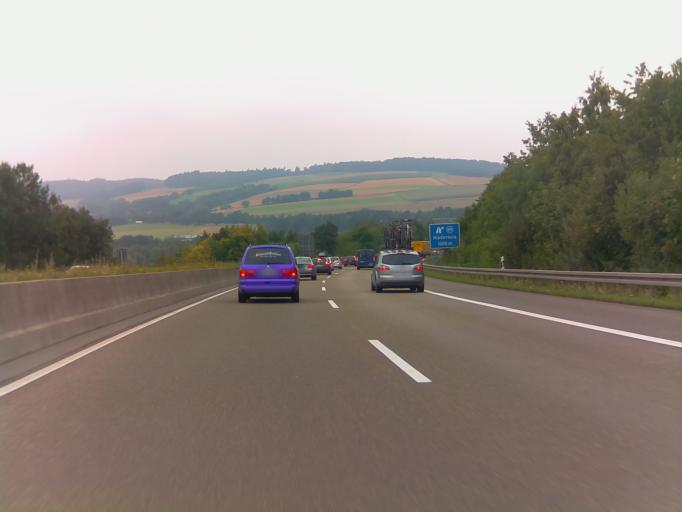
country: DE
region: Hesse
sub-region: Regierungsbezirk Kassel
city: Niederaula
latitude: 50.7654
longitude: 9.5906
